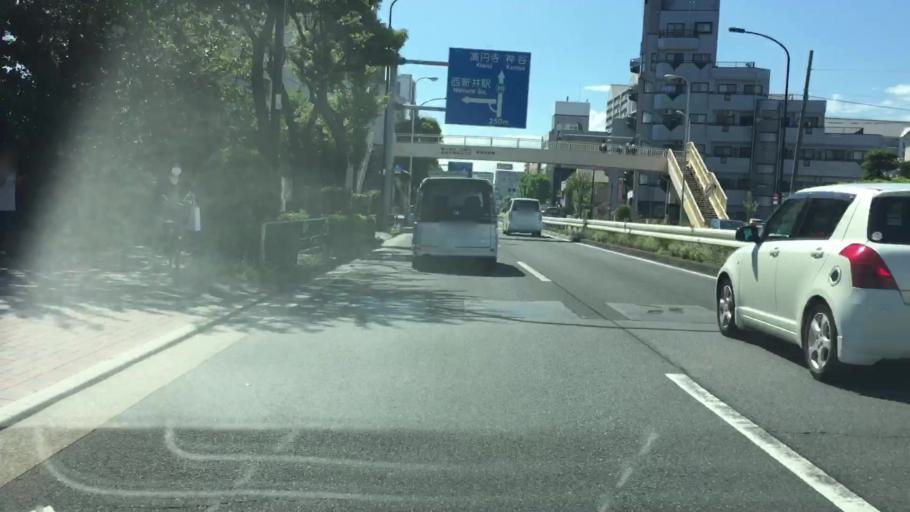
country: JP
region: Saitama
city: Soka
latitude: 35.7784
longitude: 139.7942
